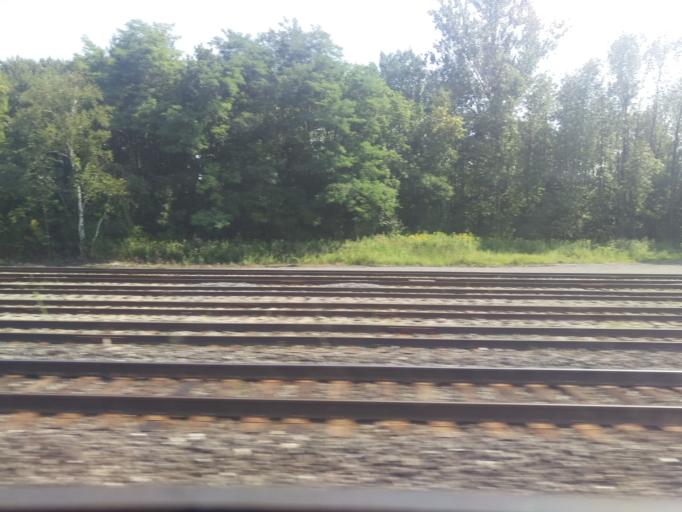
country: CA
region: Ontario
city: Brockville
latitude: 44.5851
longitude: -75.7138
